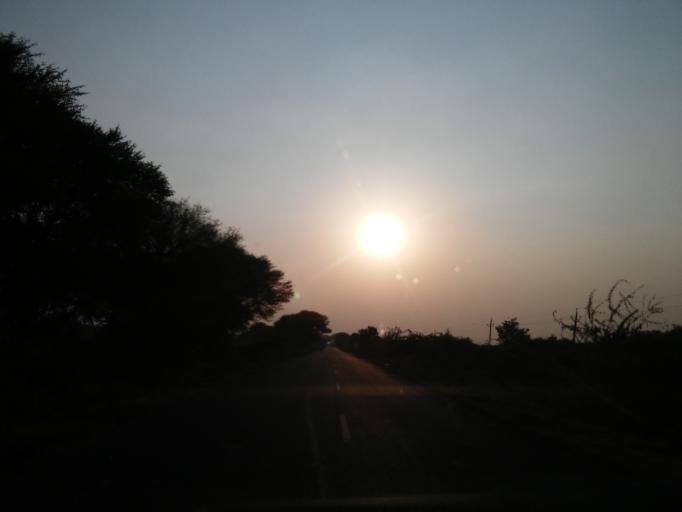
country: IN
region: Gujarat
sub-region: Ahmadabad
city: Sanand
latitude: 23.0831
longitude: 72.4120
